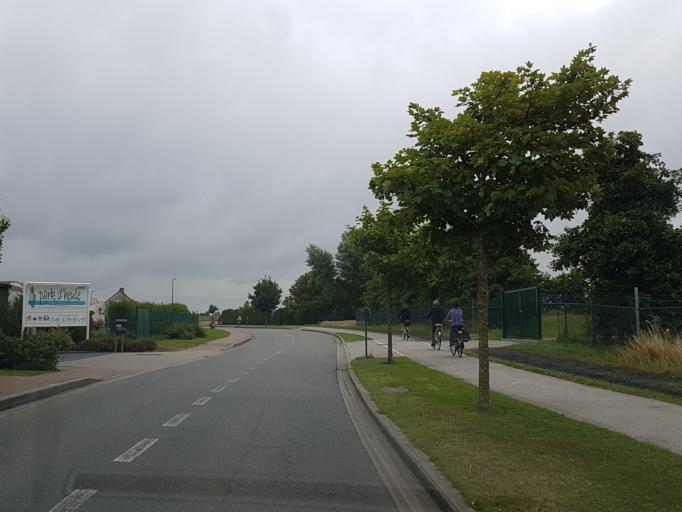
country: BE
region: Flanders
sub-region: Provincie West-Vlaanderen
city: Bredene
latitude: 51.2408
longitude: 2.9775
